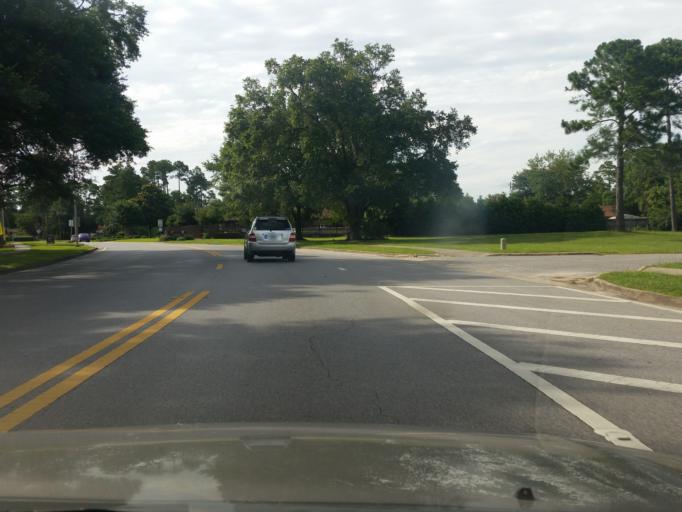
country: US
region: Florida
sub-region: Escambia County
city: Ferry Pass
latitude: 30.4852
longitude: -87.2136
